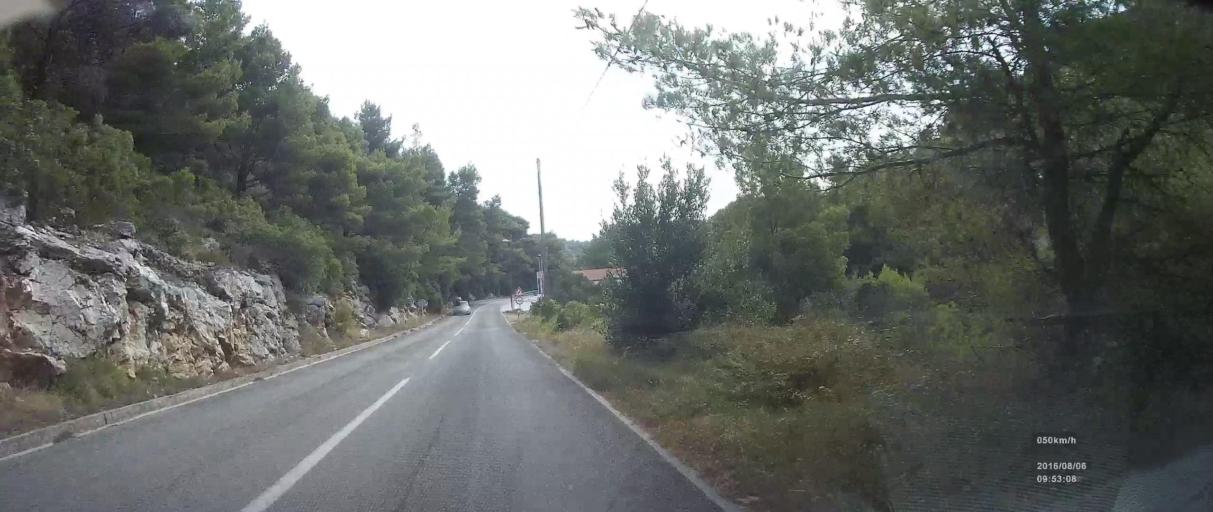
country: HR
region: Dubrovacko-Neretvanska
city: Blato
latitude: 42.7319
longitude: 17.5823
